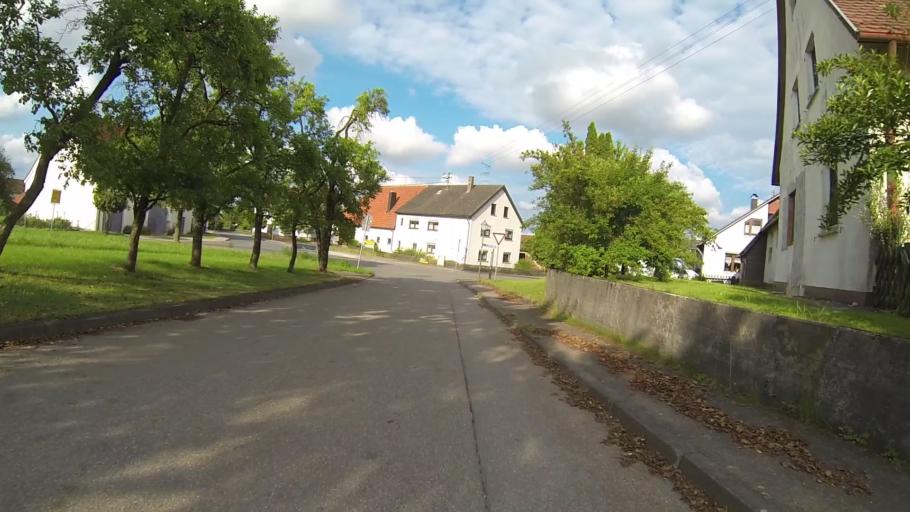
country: DE
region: Baden-Wuerttemberg
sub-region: Regierungsbezirk Stuttgart
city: Neresheim
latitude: 48.7302
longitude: 10.2919
